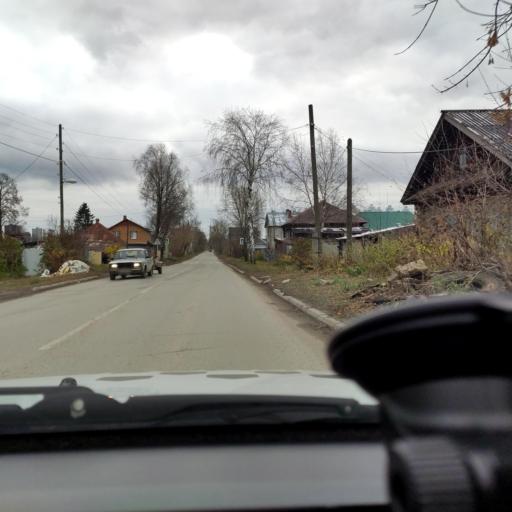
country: RU
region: Perm
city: Perm
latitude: 58.0159
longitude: 56.3161
